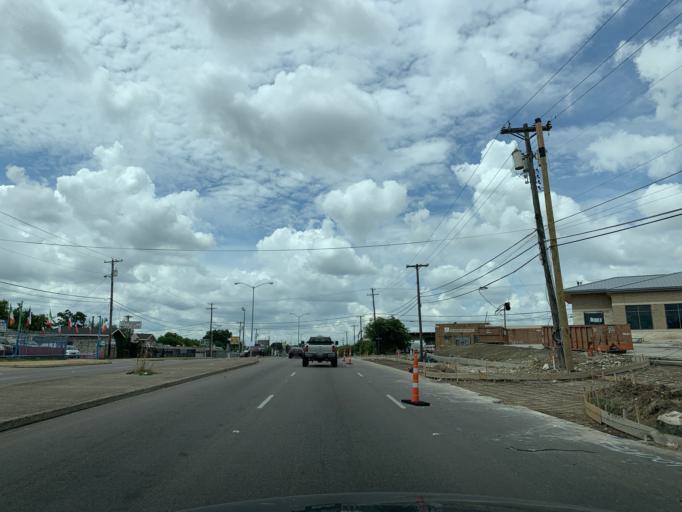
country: US
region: Texas
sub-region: Dallas County
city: Cockrell Hill
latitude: 32.7575
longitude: -96.8662
